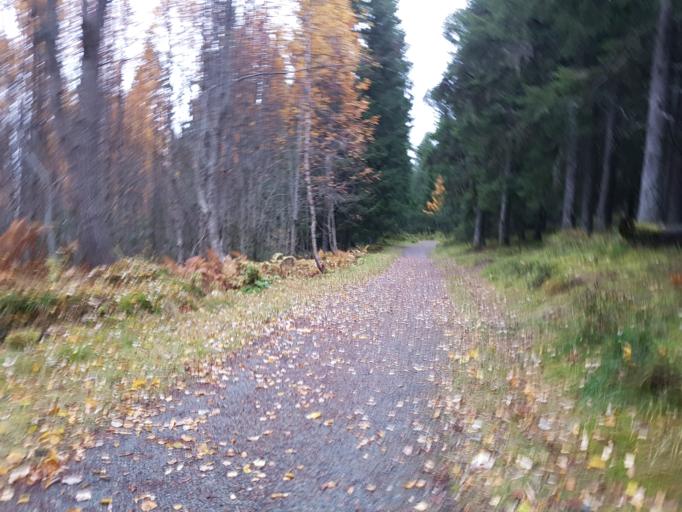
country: NO
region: Sor-Trondelag
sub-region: Trondheim
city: Trondheim
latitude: 63.3808
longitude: 10.3284
